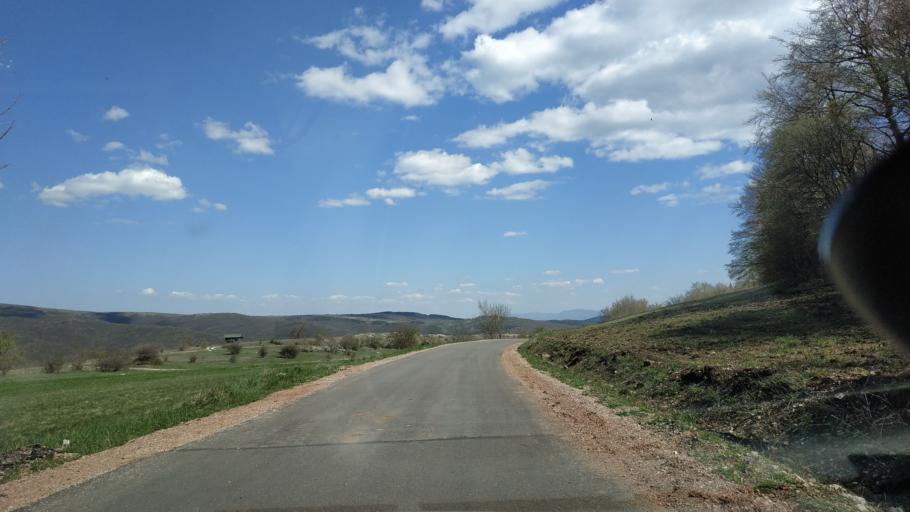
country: RS
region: Central Serbia
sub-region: Zajecarski Okrug
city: Soko Banja
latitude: 43.5833
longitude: 21.8917
